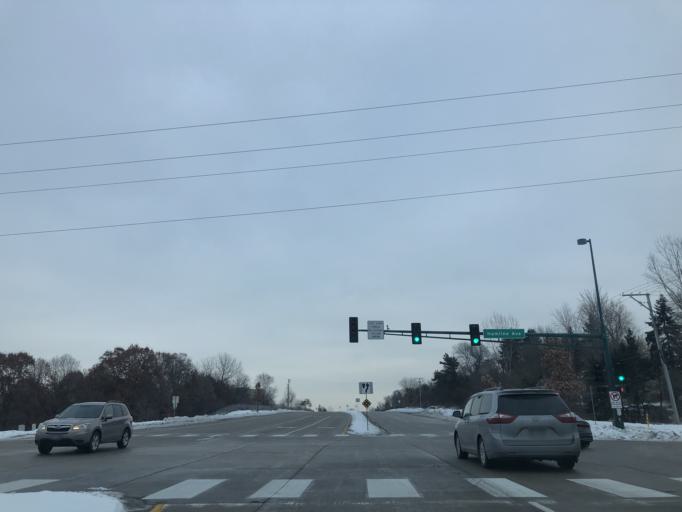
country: US
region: Minnesota
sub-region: Ramsey County
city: Shoreview
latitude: 45.0792
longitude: -93.1579
